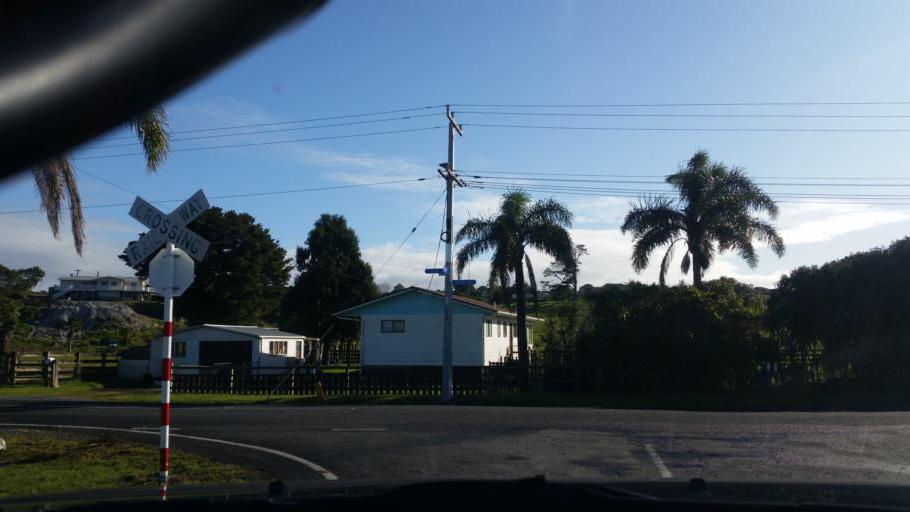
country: NZ
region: Northland
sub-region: Kaipara District
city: Dargaville
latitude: -35.9398
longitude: 173.8593
